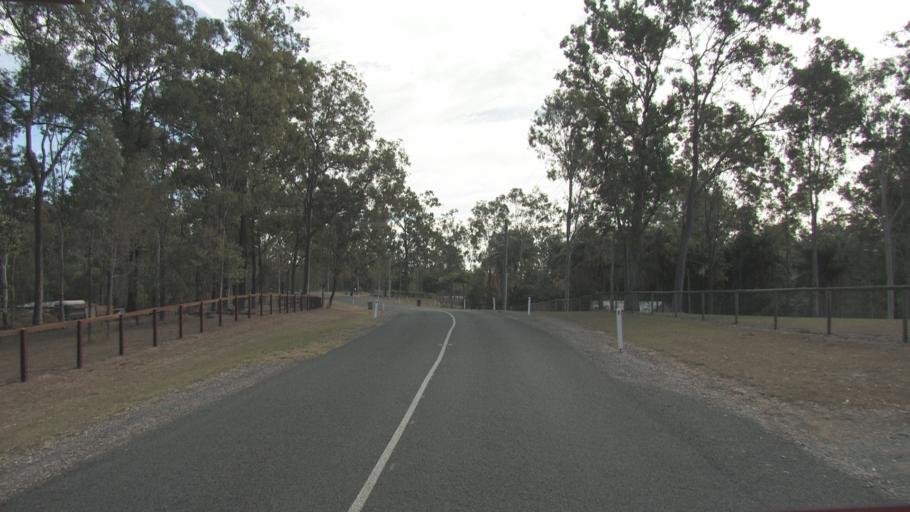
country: AU
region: Queensland
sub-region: Logan
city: North Maclean
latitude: -27.7715
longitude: 152.9680
